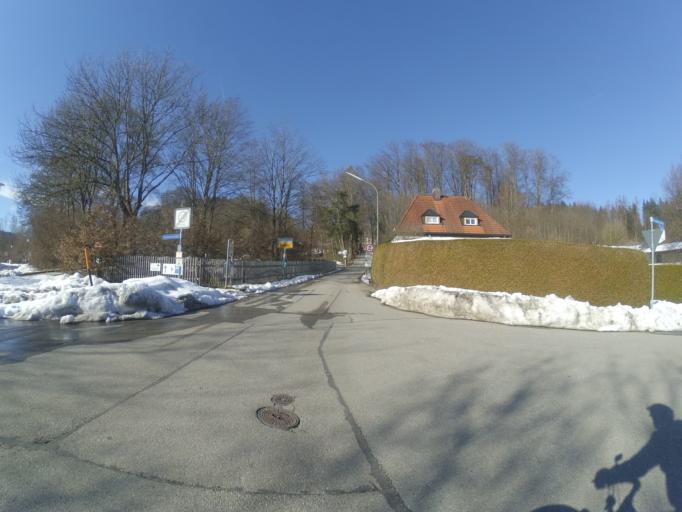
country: DE
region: Bavaria
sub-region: Upper Bavaria
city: Feldkirchen-Westerham
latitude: 47.9061
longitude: 11.8325
